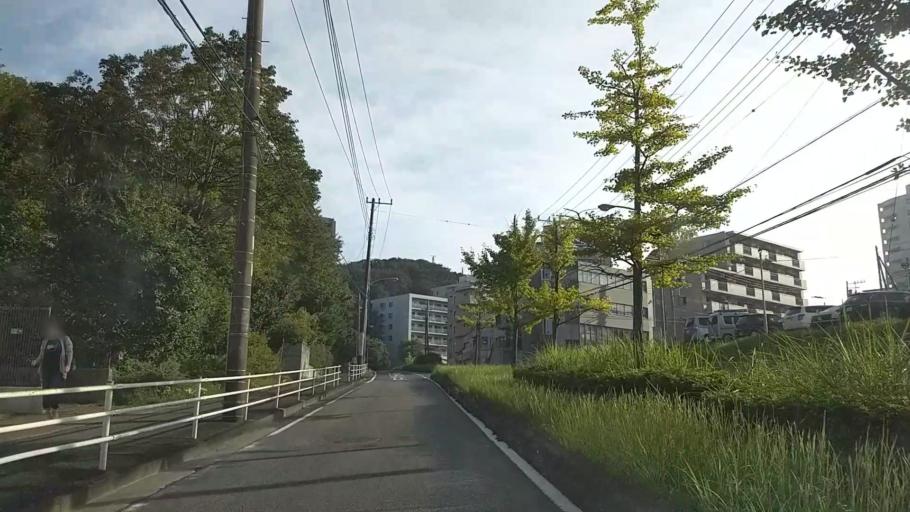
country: JP
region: Kanagawa
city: Yokohama
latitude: 35.4344
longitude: 139.5591
